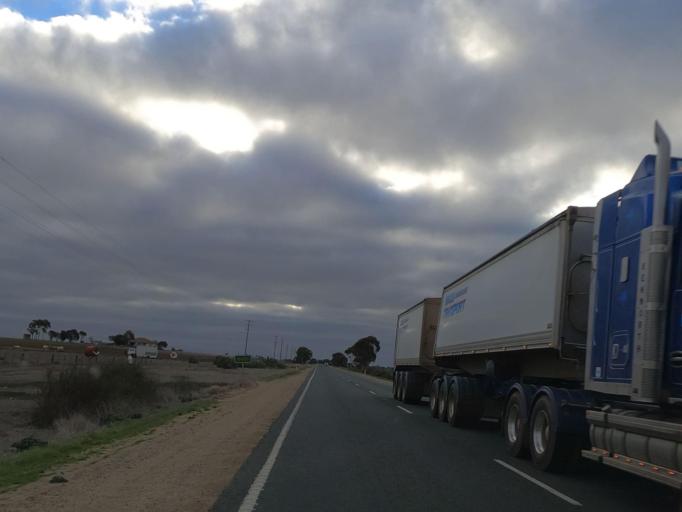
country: AU
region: Victoria
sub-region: Swan Hill
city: Swan Hill
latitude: -35.6433
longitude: 143.8316
